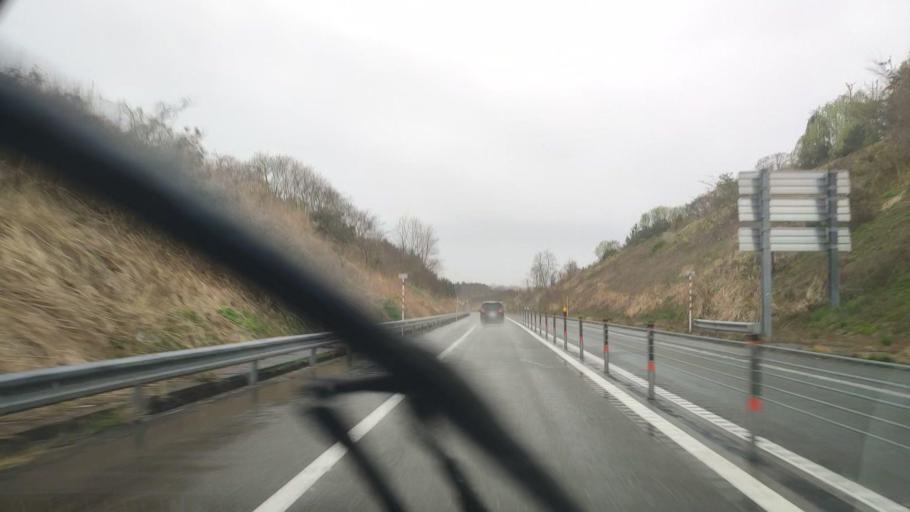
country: JP
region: Akita
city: Noshiromachi
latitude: 40.1613
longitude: 140.0368
